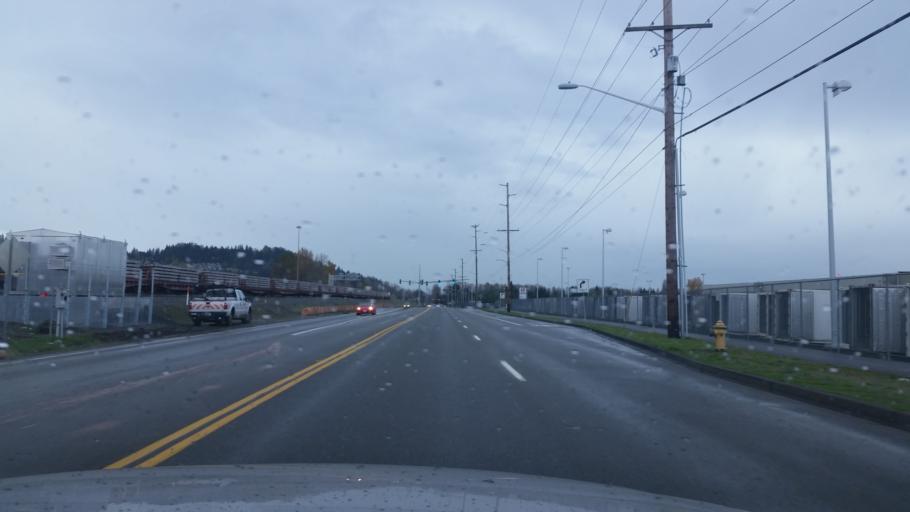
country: US
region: Washington
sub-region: King County
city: Algona
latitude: 47.2778
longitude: -122.2311
